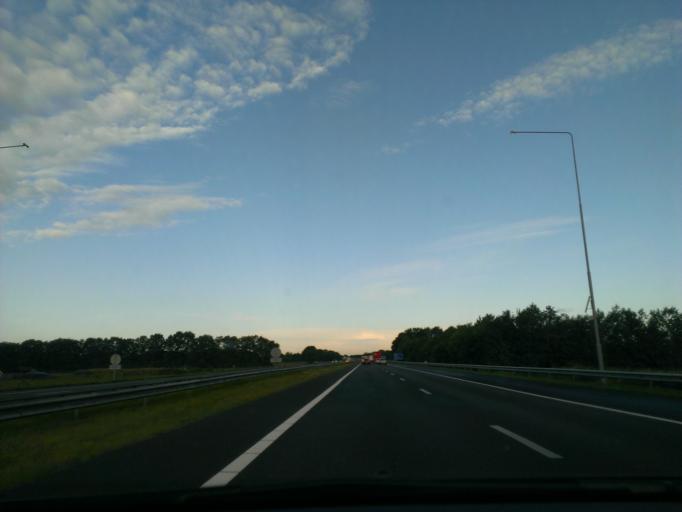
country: NL
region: Overijssel
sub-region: Gemeente Staphorst
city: Staphorst
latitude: 52.6826
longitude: 6.2840
